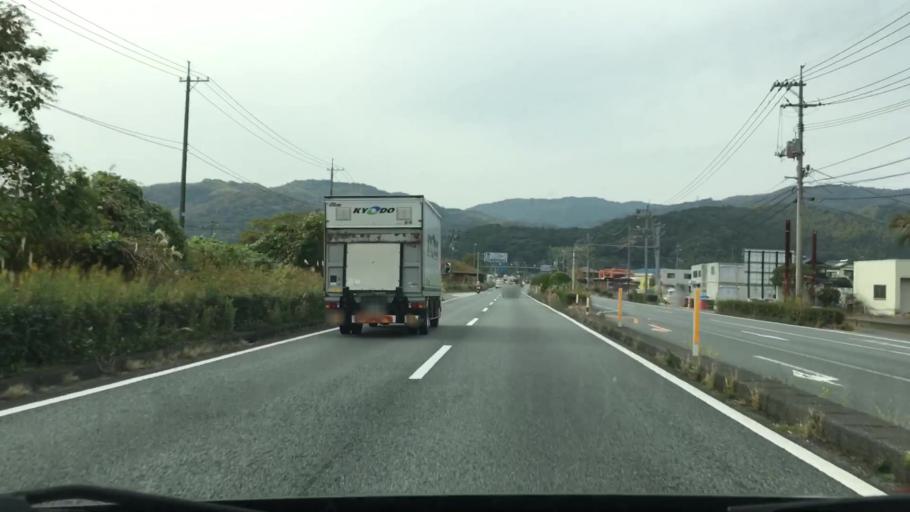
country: JP
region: Yamaguchi
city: Tokuyama
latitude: 34.0796
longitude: 131.7192
